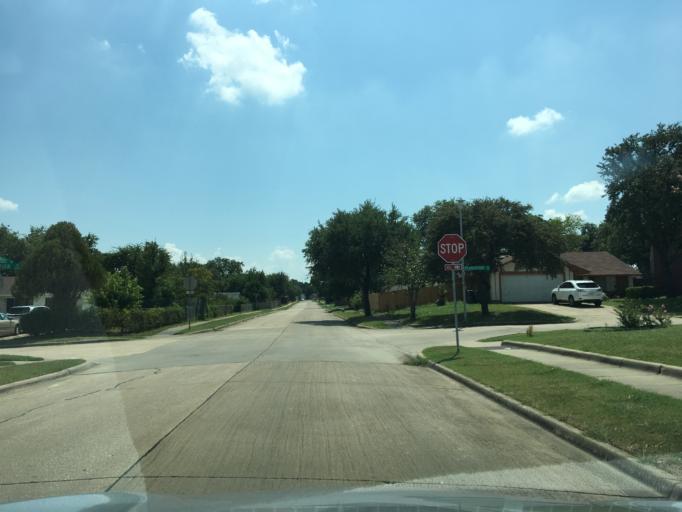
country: US
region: Texas
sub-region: Dallas County
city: Garland
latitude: 32.9426
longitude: -96.6530
